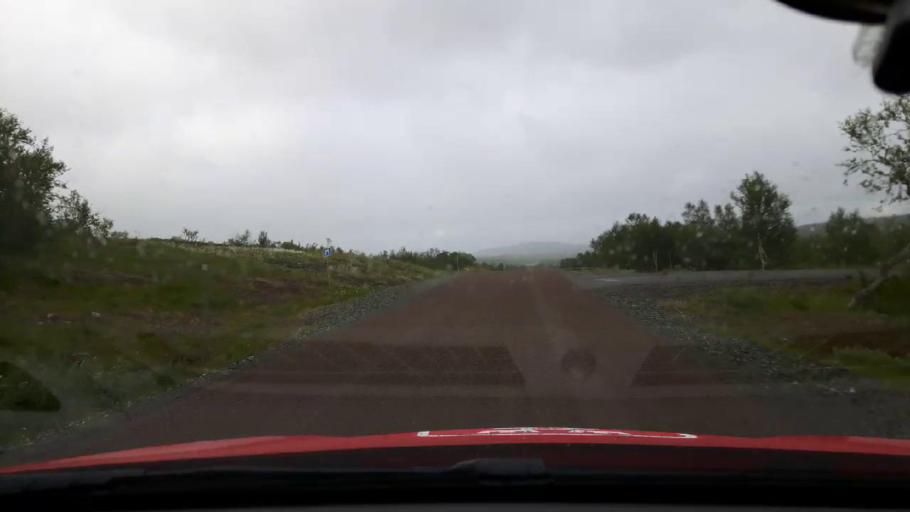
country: NO
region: Nord-Trondelag
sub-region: Meraker
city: Meraker
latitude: 63.1881
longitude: 12.3812
